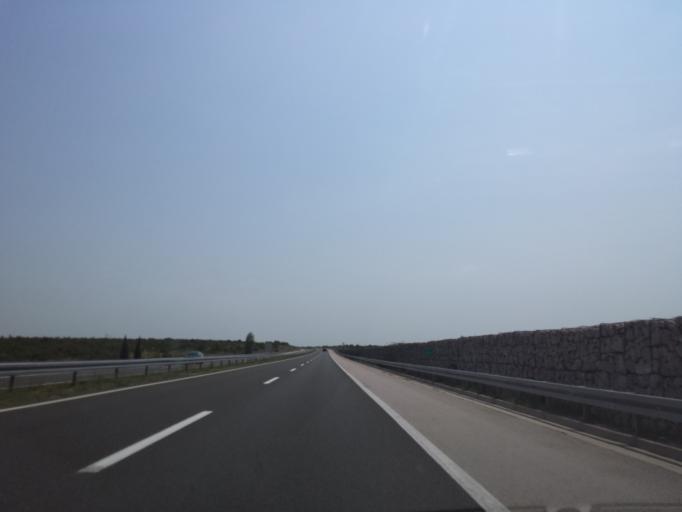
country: HR
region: Zadarska
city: Polaca
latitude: 44.0485
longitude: 15.5466
